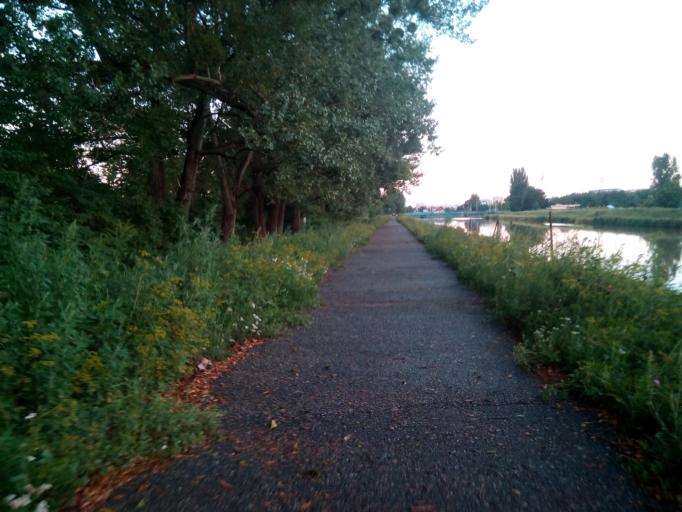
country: SK
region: Kosicky
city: Kosice
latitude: 48.7473
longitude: 21.2563
